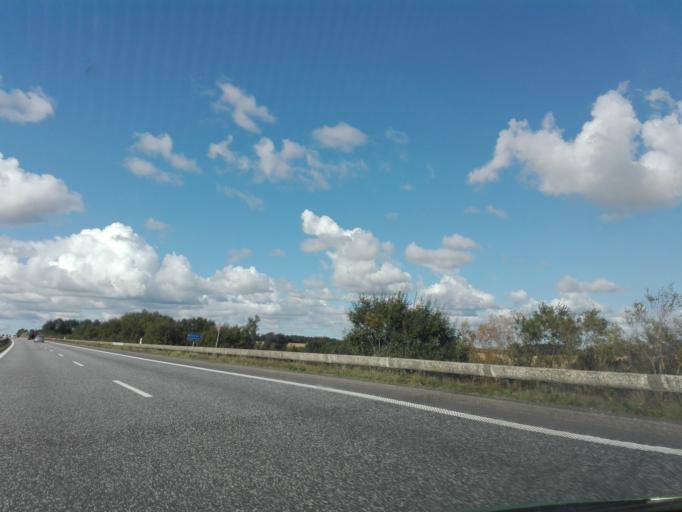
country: DK
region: Central Jutland
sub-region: Randers Kommune
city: Spentrup
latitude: 56.5240
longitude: 9.9479
